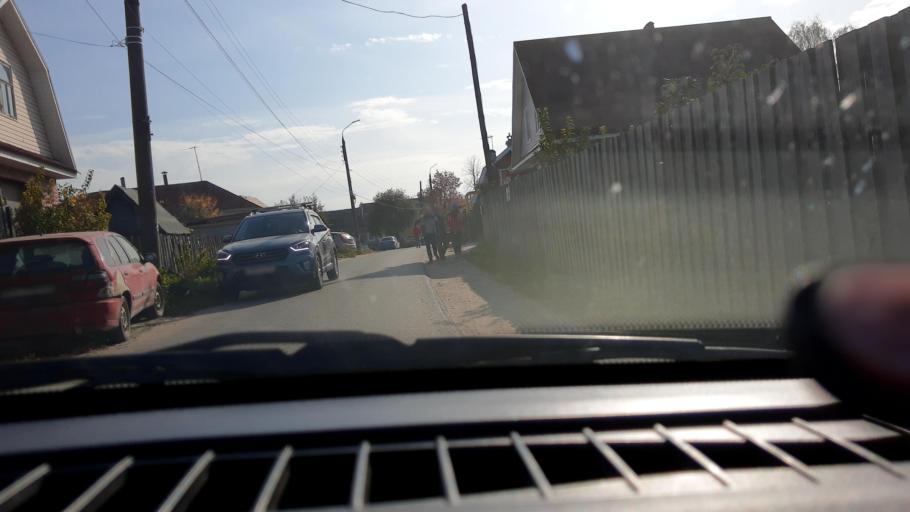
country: RU
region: Nizjnij Novgorod
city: Gorodets
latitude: 56.6408
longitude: 43.4701
